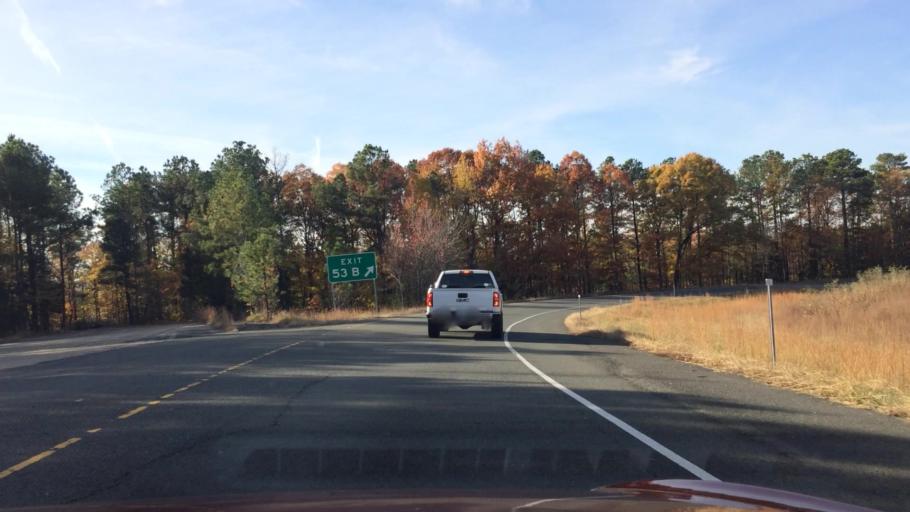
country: US
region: Virginia
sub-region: Henrico County
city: Short Pump
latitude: 37.6545
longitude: -77.6062
